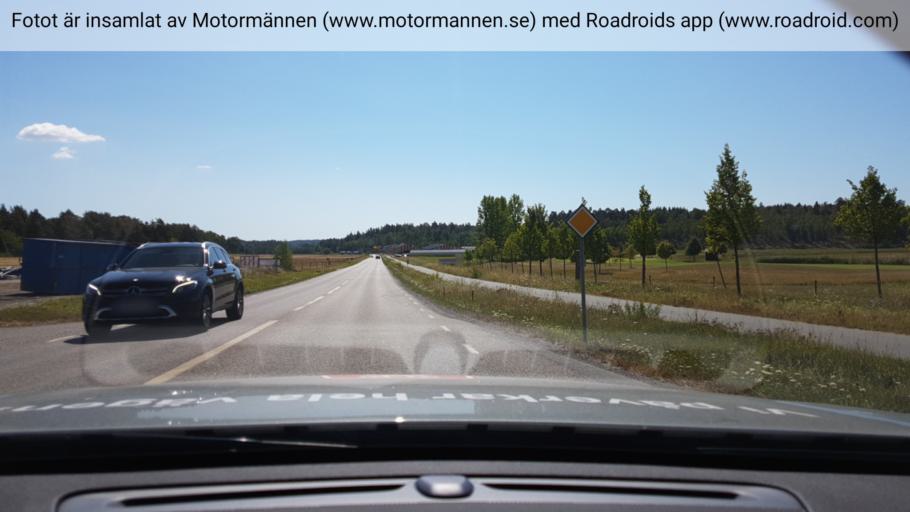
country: SE
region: Stockholm
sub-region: Ekero Kommun
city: Ekeroe
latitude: 59.3149
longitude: 17.7717
